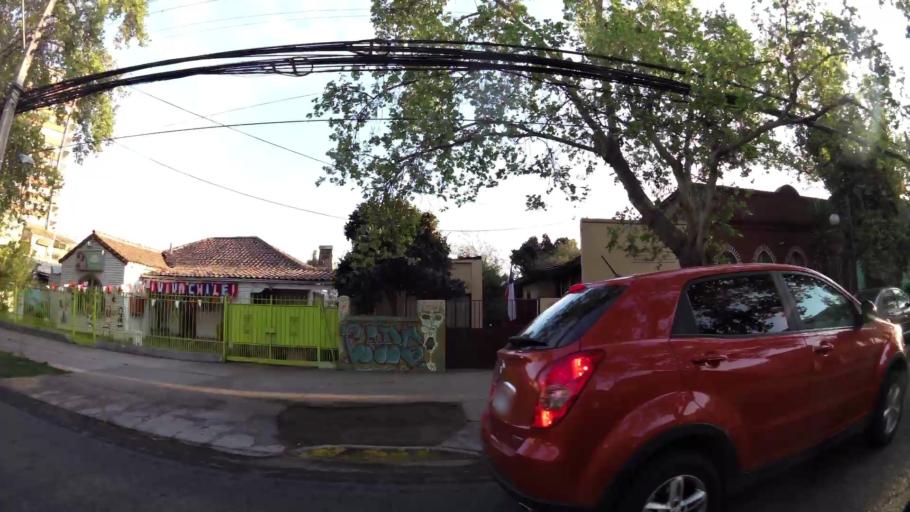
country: CL
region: Santiago Metropolitan
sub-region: Provincia de Santiago
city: Villa Presidente Frei, Nunoa, Santiago, Chile
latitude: -33.4485
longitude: -70.5925
